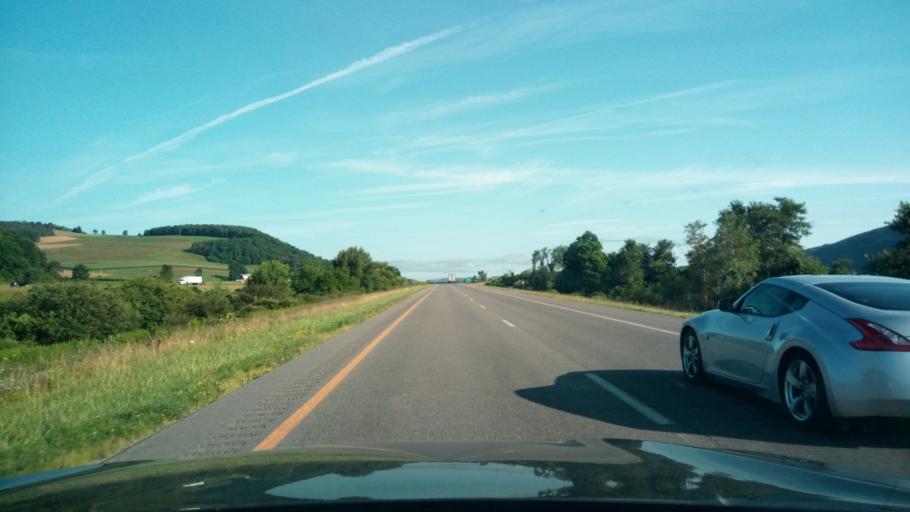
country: US
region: New York
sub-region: Steuben County
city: Wayland
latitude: 42.4555
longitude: -77.4782
